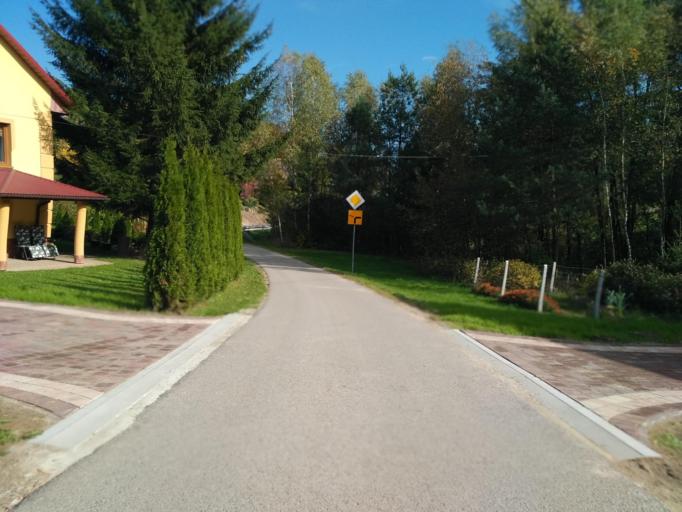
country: PL
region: Subcarpathian Voivodeship
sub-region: Powiat debicki
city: Slotowa
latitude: 49.9221
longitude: 21.2978
